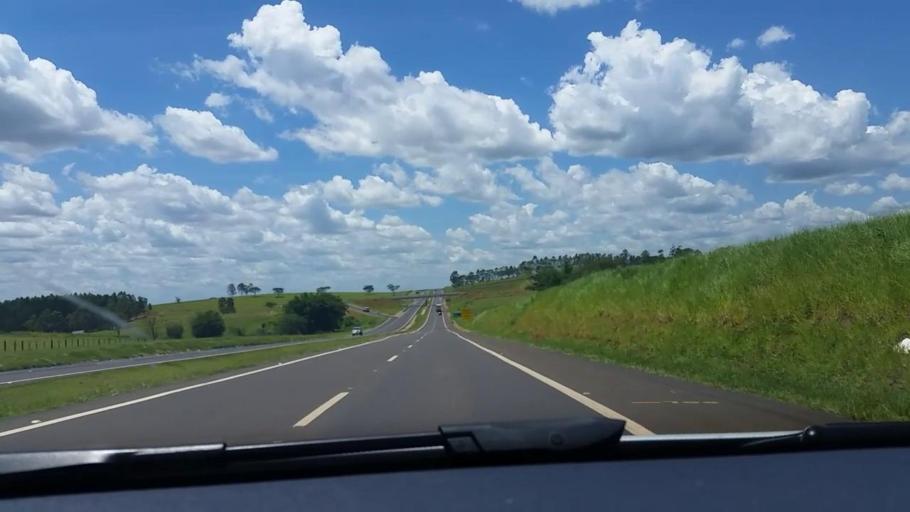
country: BR
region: Sao Paulo
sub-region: Bauru
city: Bauru
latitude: -22.4272
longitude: -49.1299
